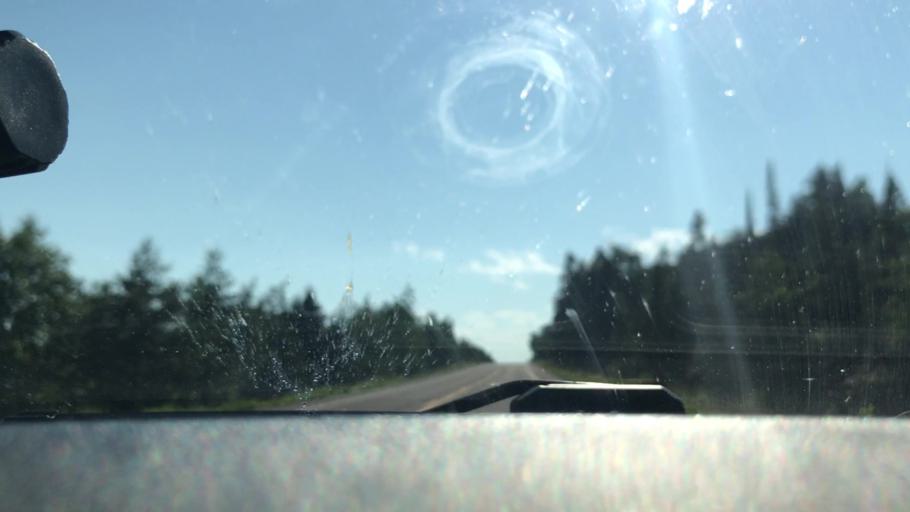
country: US
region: Minnesota
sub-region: Cook County
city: Grand Marais
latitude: 47.8286
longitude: -90.0001
